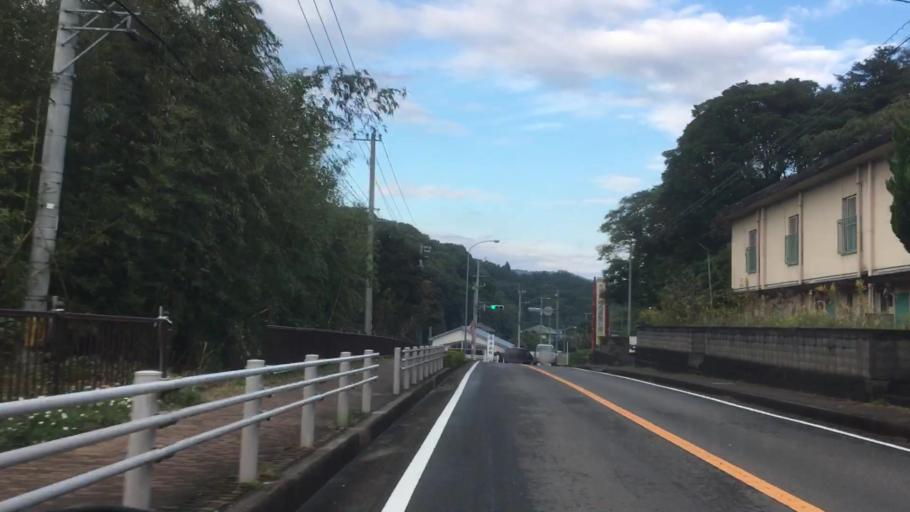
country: JP
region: Nagasaki
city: Togitsu
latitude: 32.9389
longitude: 129.6537
